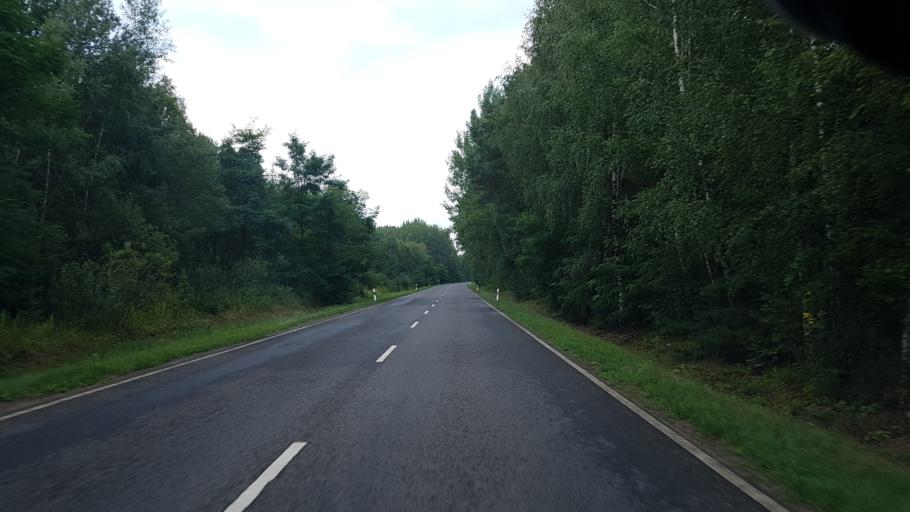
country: DE
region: Brandenburg
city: Lauchhammer
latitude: 51.5013
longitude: 13.7413
